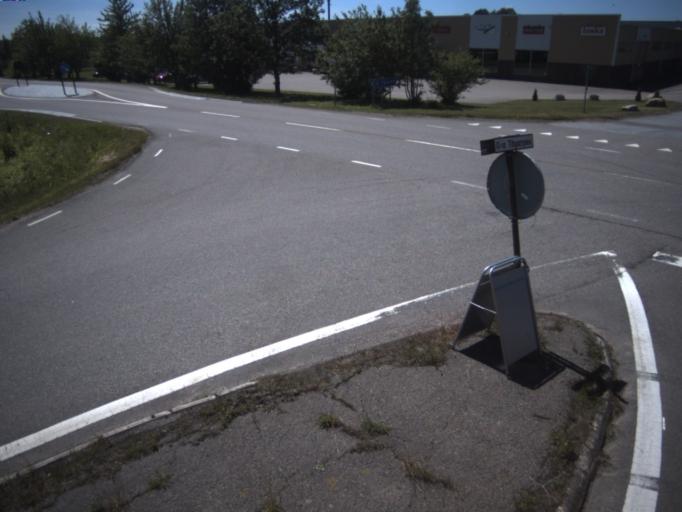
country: SE
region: Skane
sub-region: Helsingborg
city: Morarp
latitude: 56.0511
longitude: 12.8805
